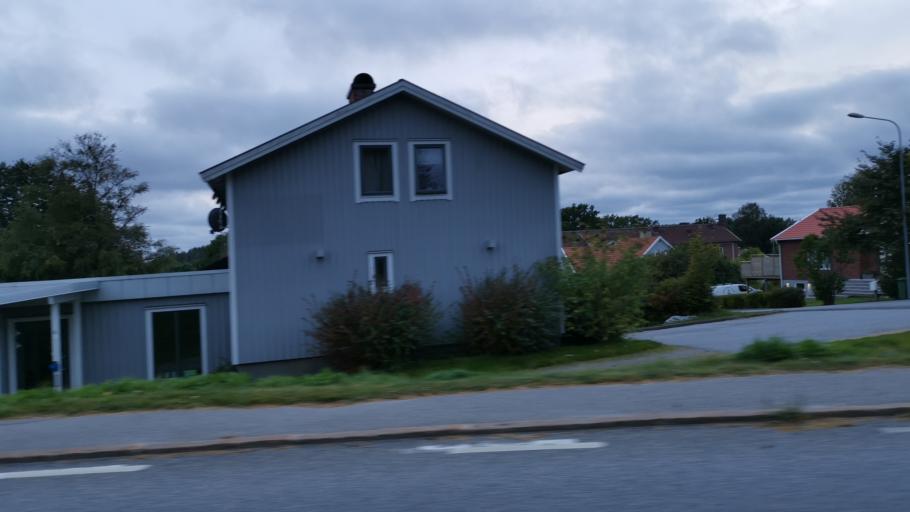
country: SE
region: Vaestra Goetaland
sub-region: Tanums Kommun
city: Tanumshede
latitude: 58.7205
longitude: 11.3261
